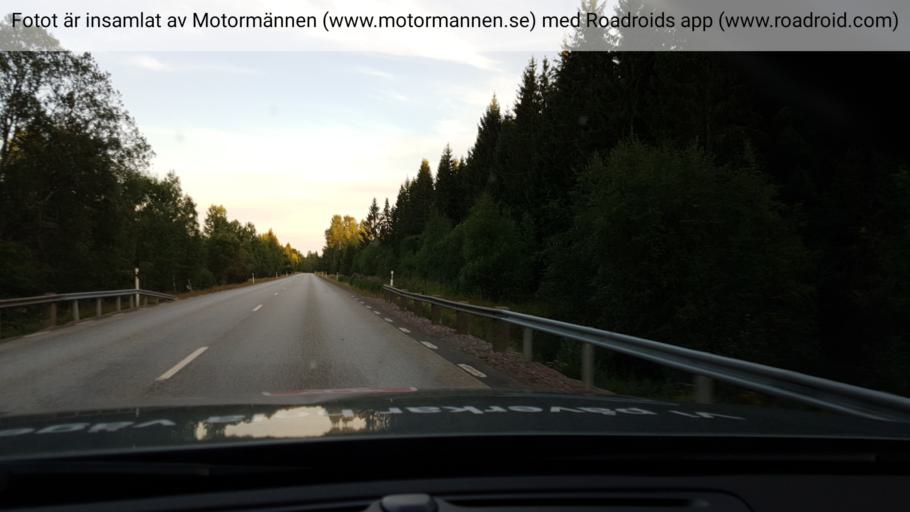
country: SE
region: Vaermland
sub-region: Storfors Kommun
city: Storfors
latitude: 59.5279
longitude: 14.2971
